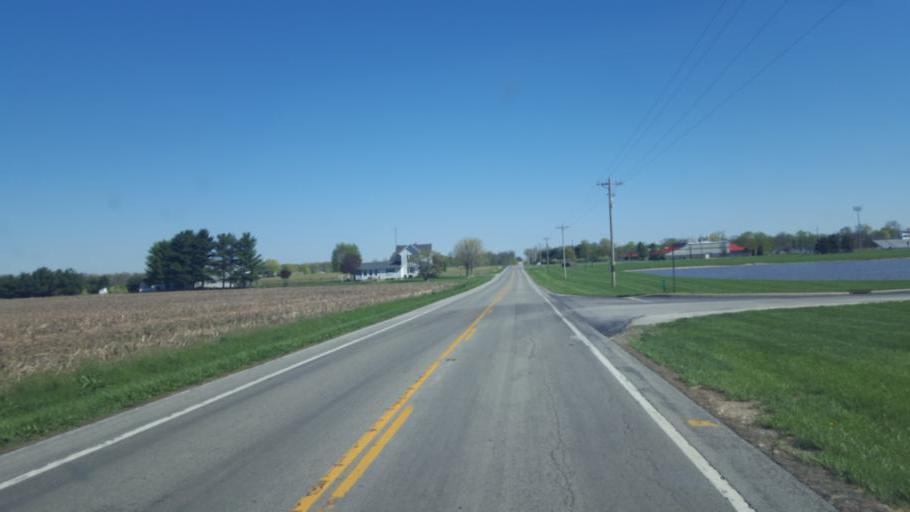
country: US
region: Ohio
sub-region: Seneca County
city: Tiffin
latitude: 40.9841
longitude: -83.1703
